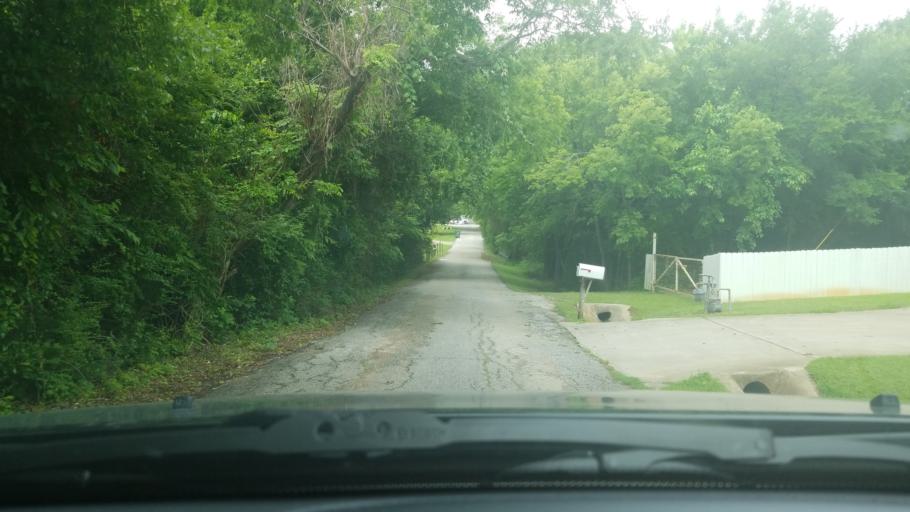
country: US
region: Texas
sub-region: Denton County
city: Lake Dallas
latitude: 33.1151
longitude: -97.0185
